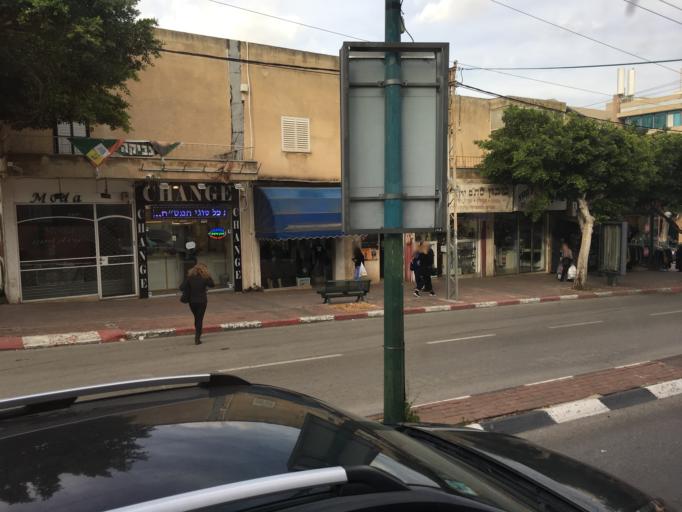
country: IL
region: Central District
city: Kfar Saba
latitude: 32.1754
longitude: 34.9080
